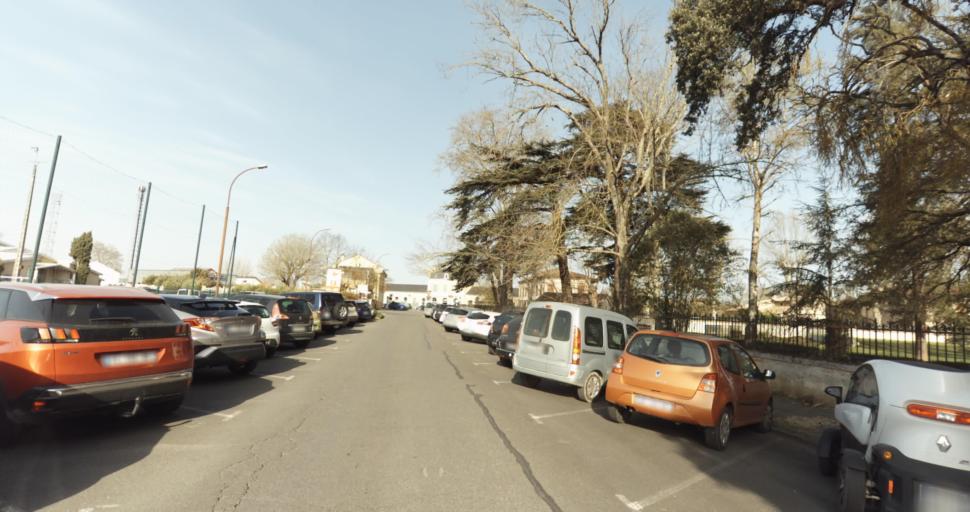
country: FR
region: Midi-Pyrenees
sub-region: Departement du Tarn
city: Saint-Sulpice-la-Pointe
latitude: 43.7747
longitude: 1.6824
